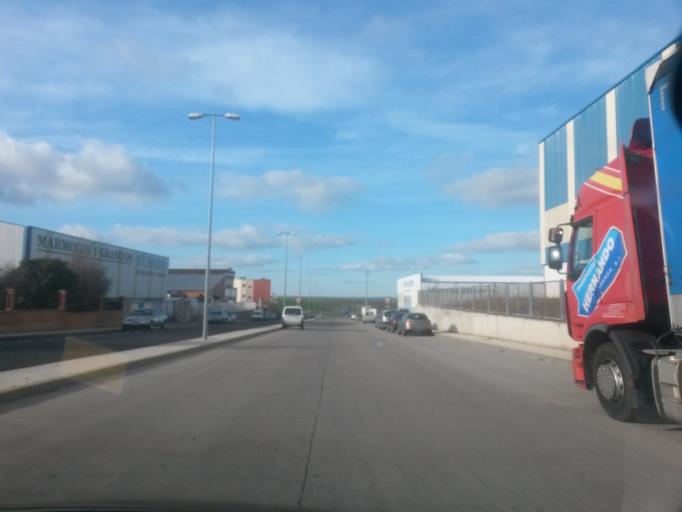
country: ES
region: Castille and Leon
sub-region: Provincia de Salamanca
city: Castellanos de Moriscos
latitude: 41.0082
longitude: -5.6096
